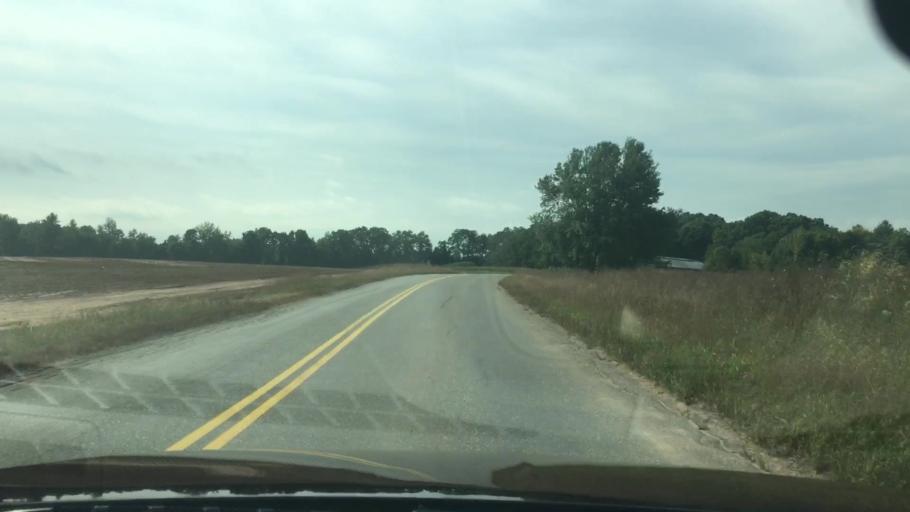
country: US
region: Connecticut
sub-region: Hartford County
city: Broad Brook
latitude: 41.8705
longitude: -72.5614
